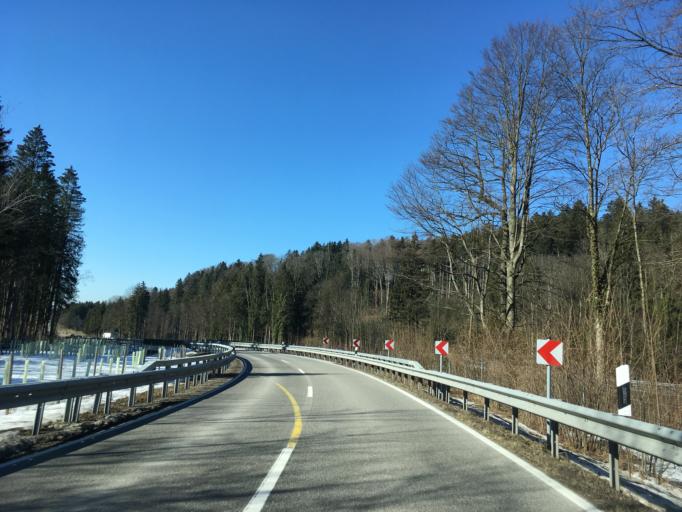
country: DE
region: Bavaria
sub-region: Upper Bavaria
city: Frasdorf
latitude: 47.7979
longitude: 12.2543
